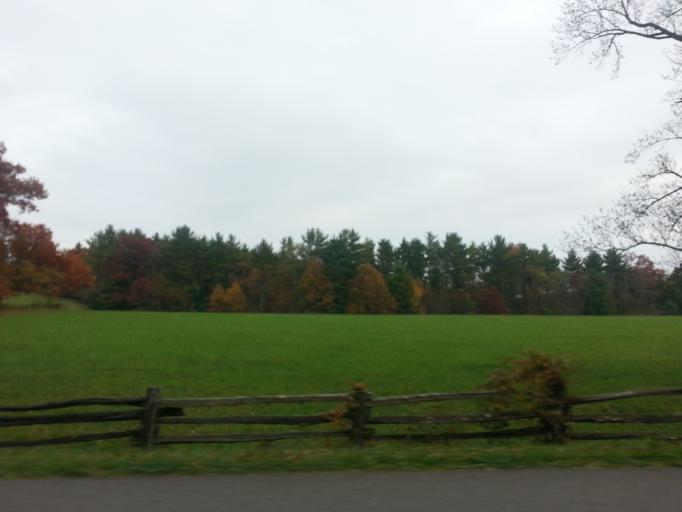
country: US
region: North Carolina
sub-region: Ashe County
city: Jefferson
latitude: 36.3546
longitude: -81.3723
